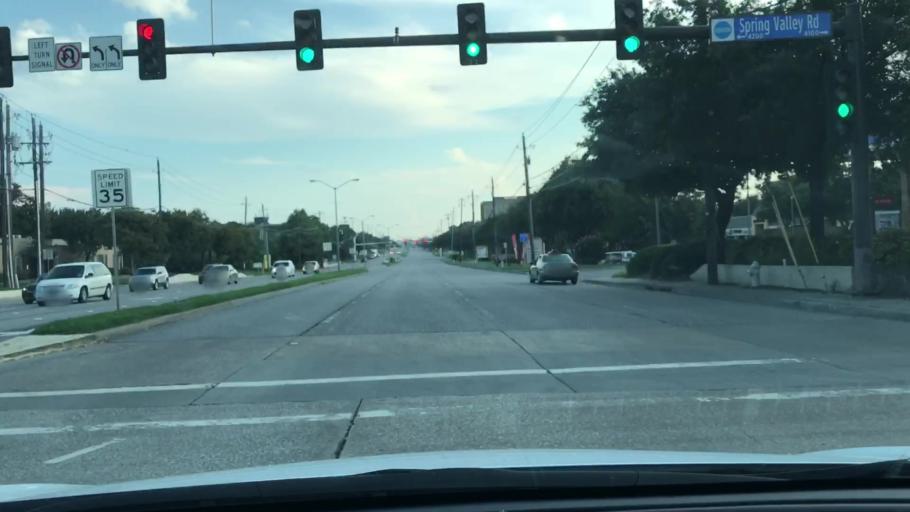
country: US
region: Texas
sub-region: Dallas County
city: Addison
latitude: 32.9399
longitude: -96.8390
